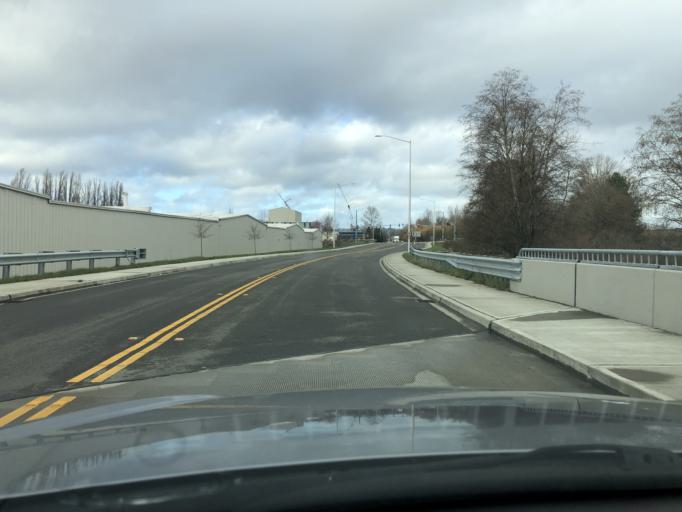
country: US
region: Washington
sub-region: King County
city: Kent
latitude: 47.4249
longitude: -122.2445
